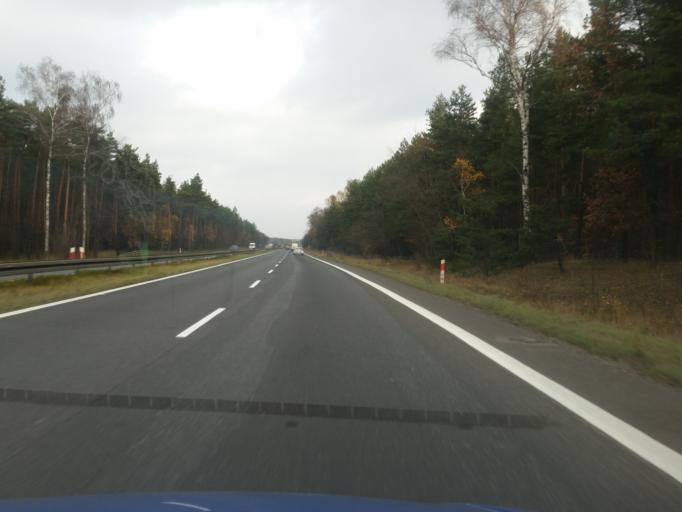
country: PL
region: Silesian Voivodeship
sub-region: Powiat bedzinski
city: Siewierz
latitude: 50.5262
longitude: 19.1924
